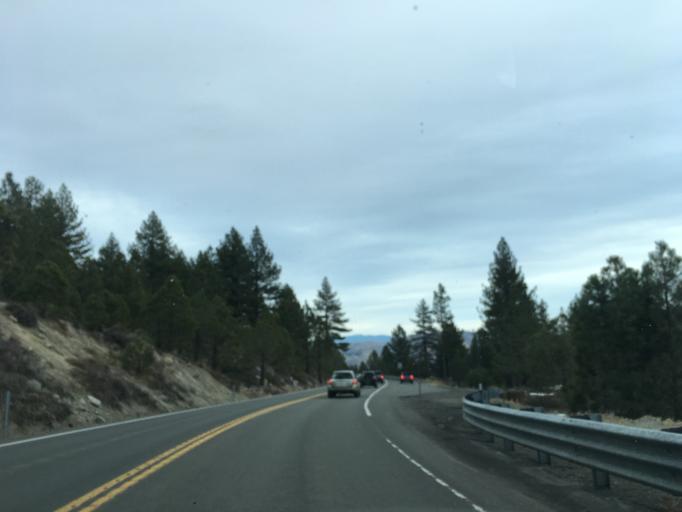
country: US
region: Nevada
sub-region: Washoe County
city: Incline Village
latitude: 39.3394
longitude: -119.8599
